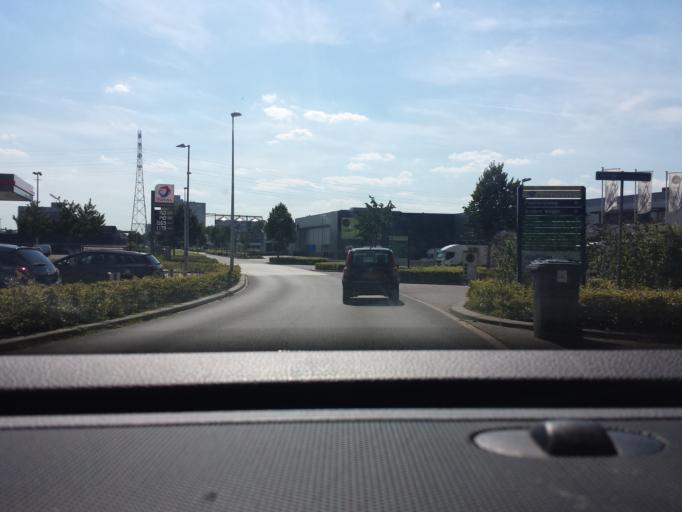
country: NL
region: Gelderland
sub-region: Gemeente Doetinchem
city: Doetinchem
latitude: 51.9751
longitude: 6.2696
